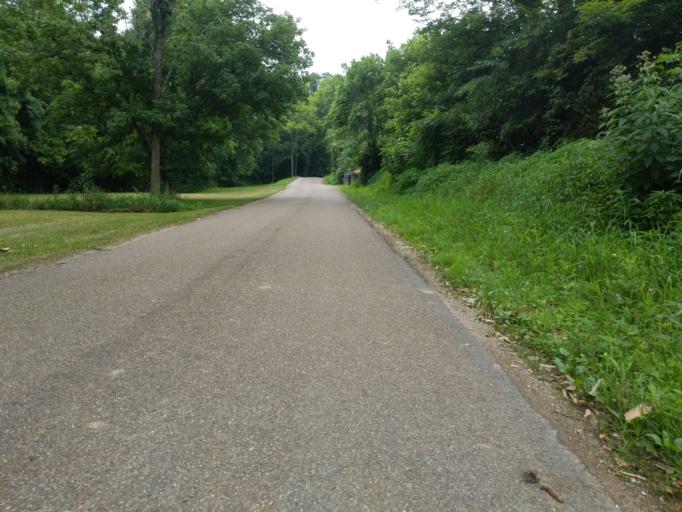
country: US
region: Ohio
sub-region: Athens County
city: The Plains
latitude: 39.3817
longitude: -82.1443
